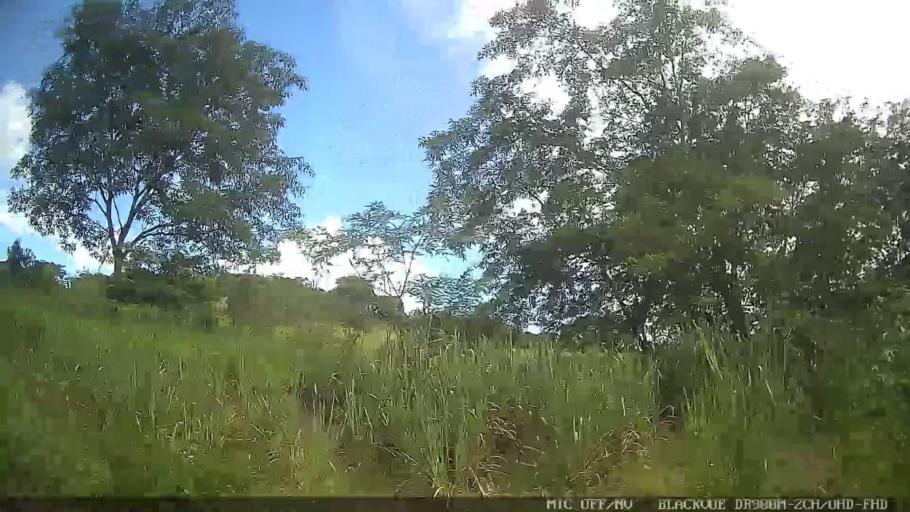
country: BR
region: Sao Paulo
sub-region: Conchas
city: Conchas
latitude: -23.0212
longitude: -48.0176
